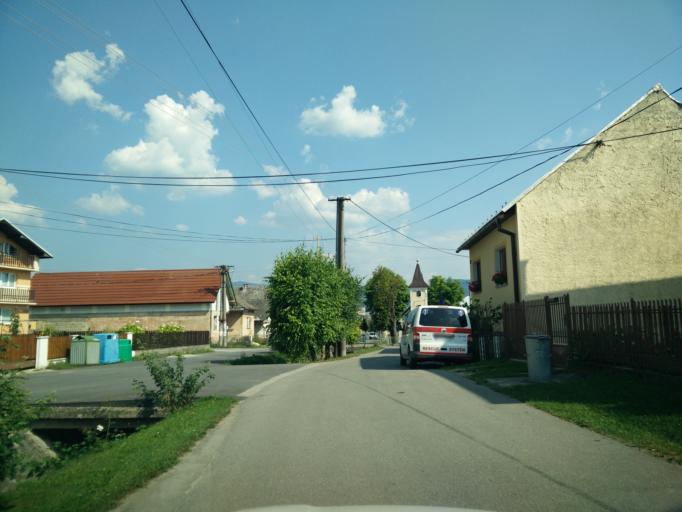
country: SK
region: Zilinsky
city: Rajec
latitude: 49.1112
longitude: 18.6353
